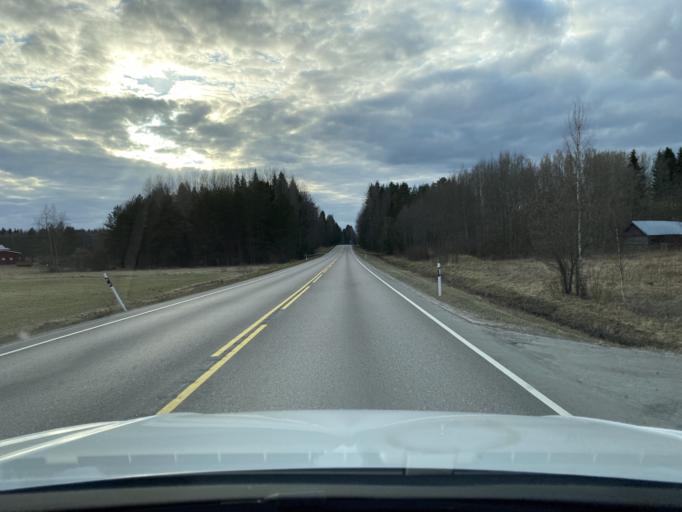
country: FI
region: Haeme
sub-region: Haemeenlinna
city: Renko
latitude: 60.7905
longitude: 24.1221
